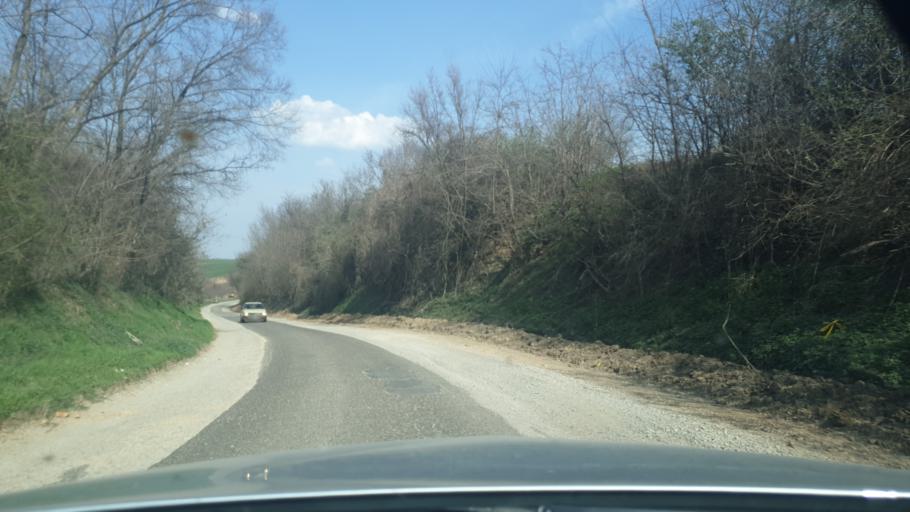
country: RS
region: Autonomna Pokrajina Vojvodina
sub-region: Sremski Okrug
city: Irig
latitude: 45.0987
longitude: 19.8869
